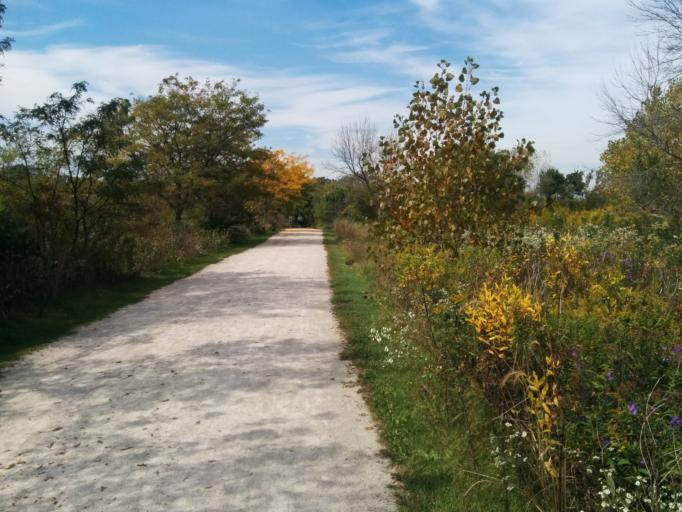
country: US
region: Illinois
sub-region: DuPage County
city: Carol Stream
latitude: 41.9420
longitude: -88.1772
